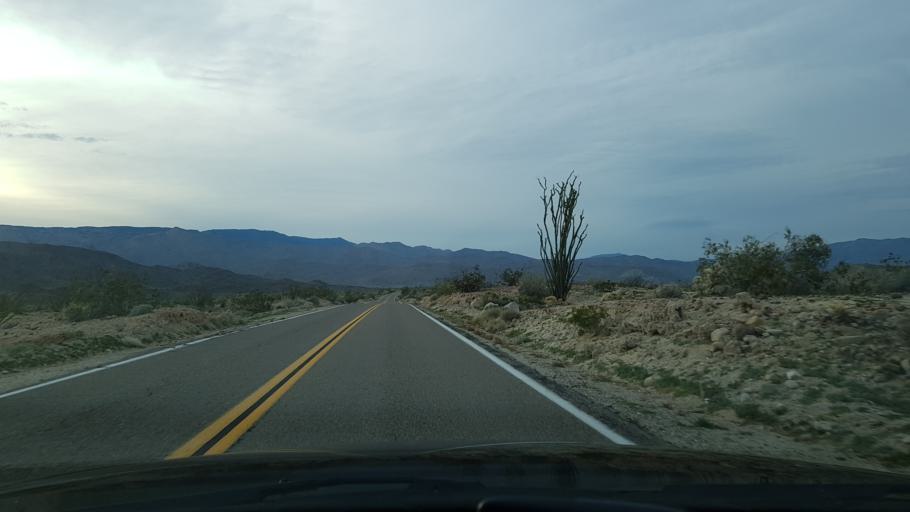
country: MX
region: Baja California
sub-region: Tecate
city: Cereso del Hongo
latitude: 32.8218
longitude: -116.1559
